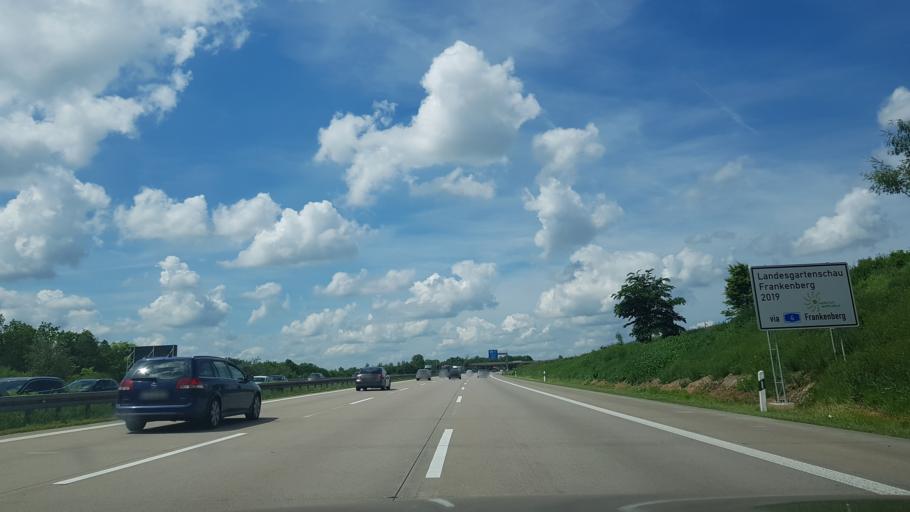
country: DE
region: Saxony
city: Reinsberg
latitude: 51.0599
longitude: 13.4036
